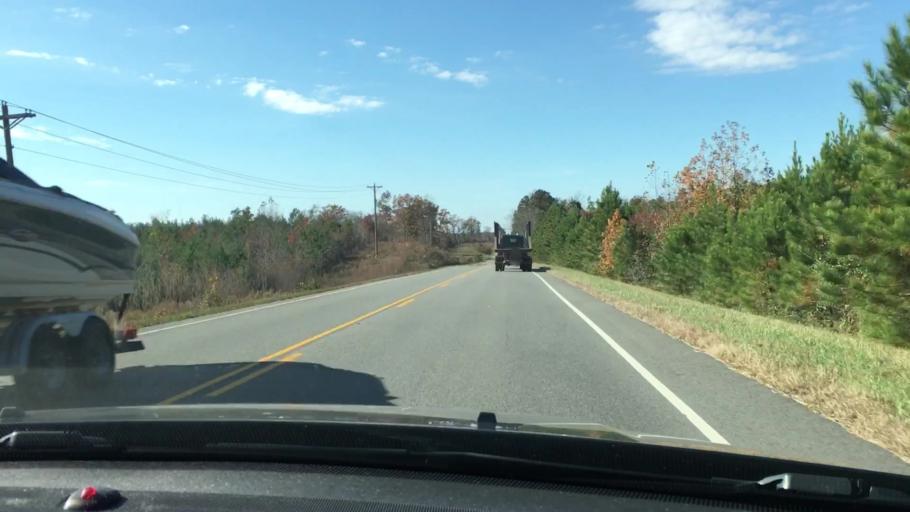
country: US
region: Virginia
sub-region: King William County
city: Central Garage
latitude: 37.7909
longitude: -77.2236
